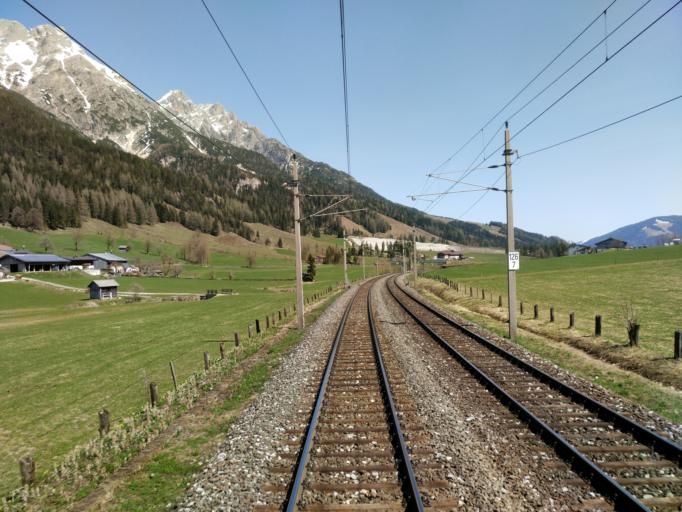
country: AT
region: Tyrol
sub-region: Politischer Bezirk Kitzbuhel
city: Hochfilzen
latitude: 47.4543
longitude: 12.6646
